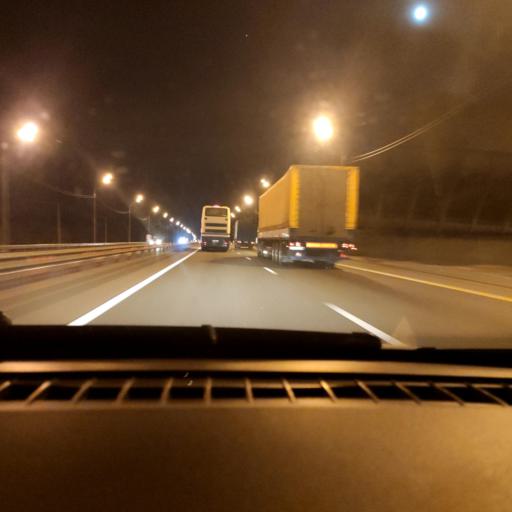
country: RU
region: Lipetsk
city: Khlevnoye
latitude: 52.2216
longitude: 39.1189
